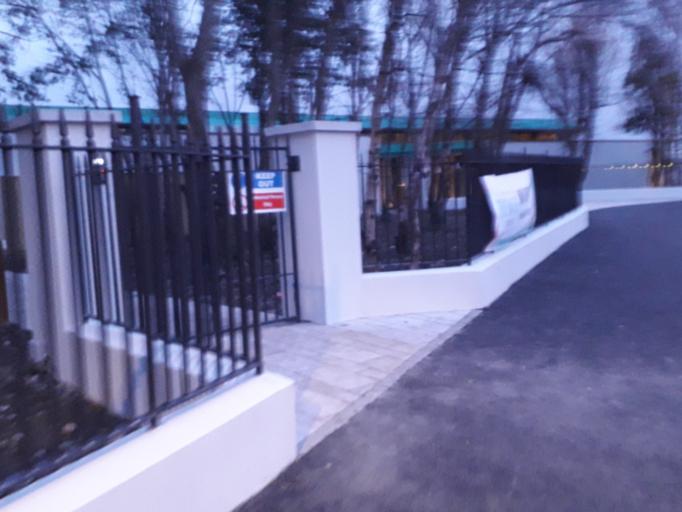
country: IE
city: Killester
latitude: 53.3600
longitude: -6.2047
